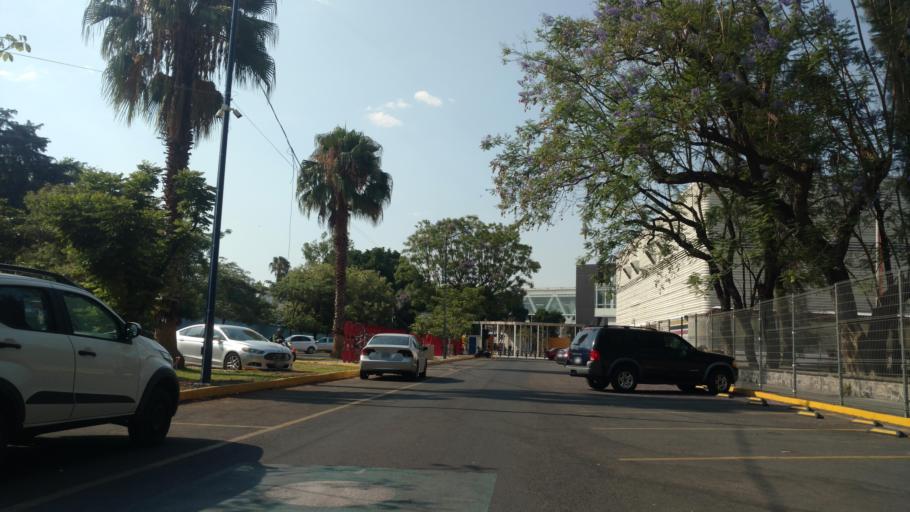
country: MX
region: Jalisco
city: Tlaquepaque
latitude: 20.6581
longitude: -103.3241
